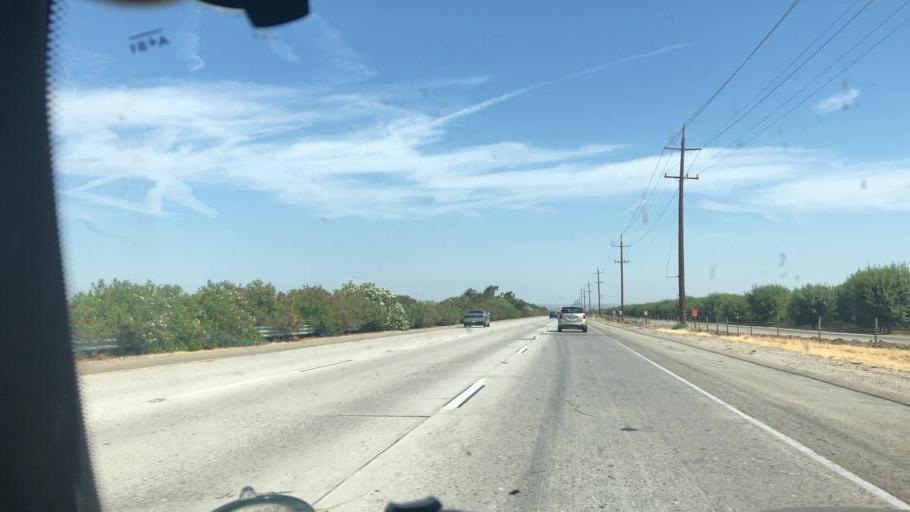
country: US
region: California
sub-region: Kern County
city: Weedpatch
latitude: 35.0344
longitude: -118.9603
